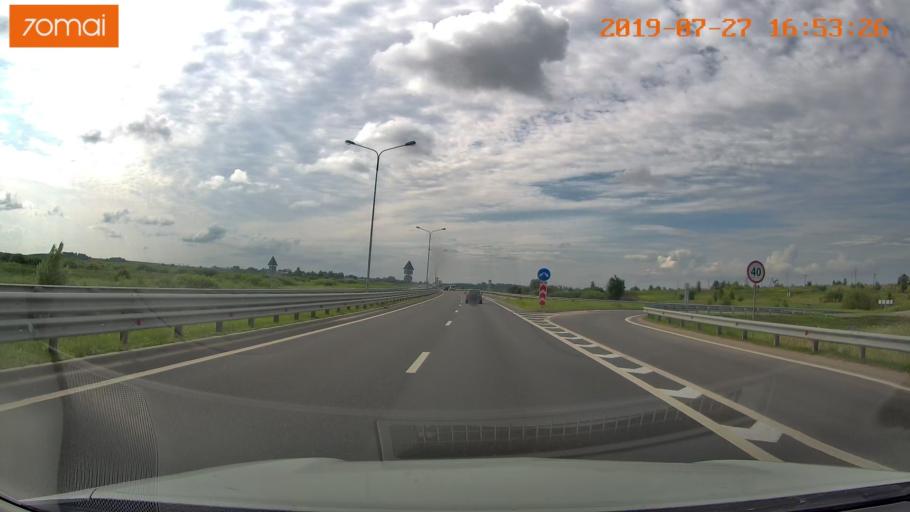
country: RU
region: Kaliningrad
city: Bol'shoe Isakovo
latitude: 54.6878
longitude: 20.8324
